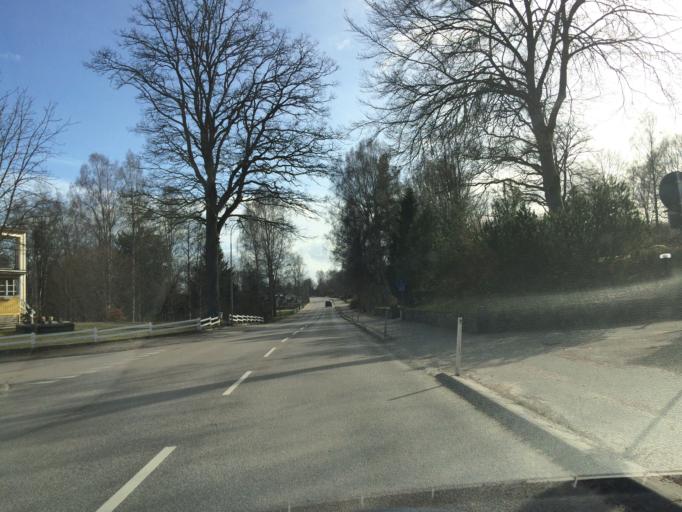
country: SE
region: Kronoberg
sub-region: Almhults Kommun
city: AElmhult
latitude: 56.5589
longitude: 14.1306
